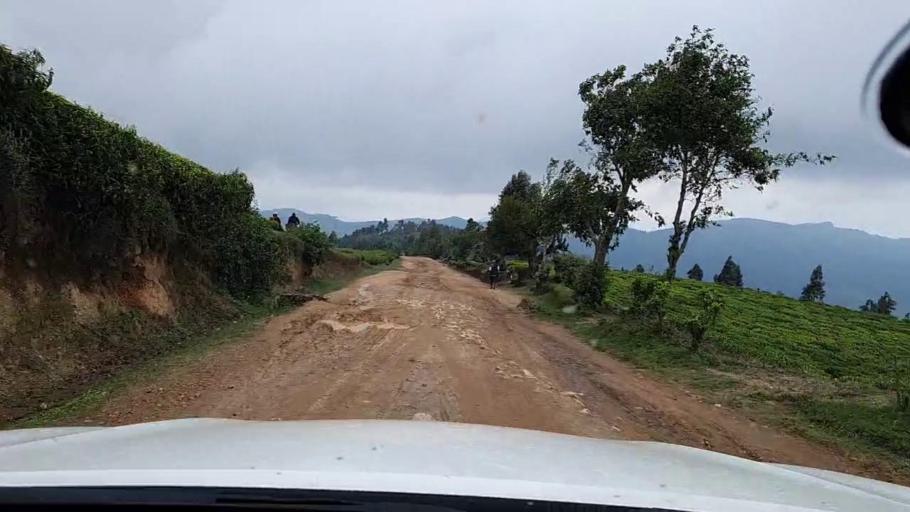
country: RW
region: Western Province
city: Kibuye
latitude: -2.2428
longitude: 29.3470
